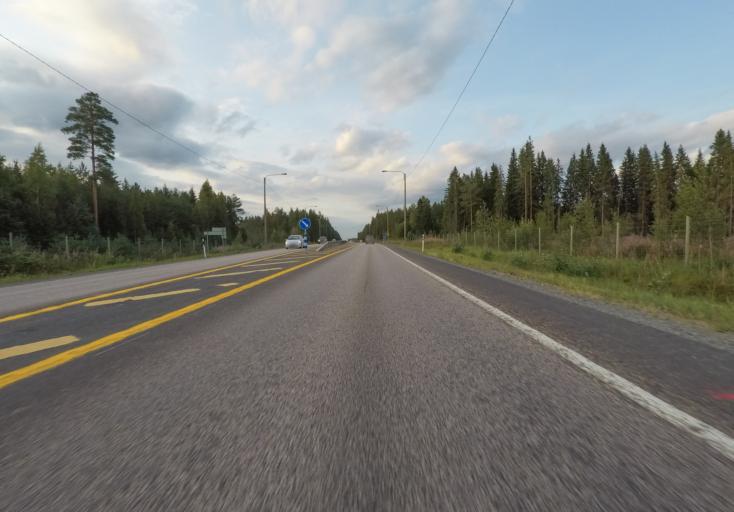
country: FI
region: Paijanne Tavastia
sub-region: Lahti
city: Hartola
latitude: 61.5276
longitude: 26.0061
